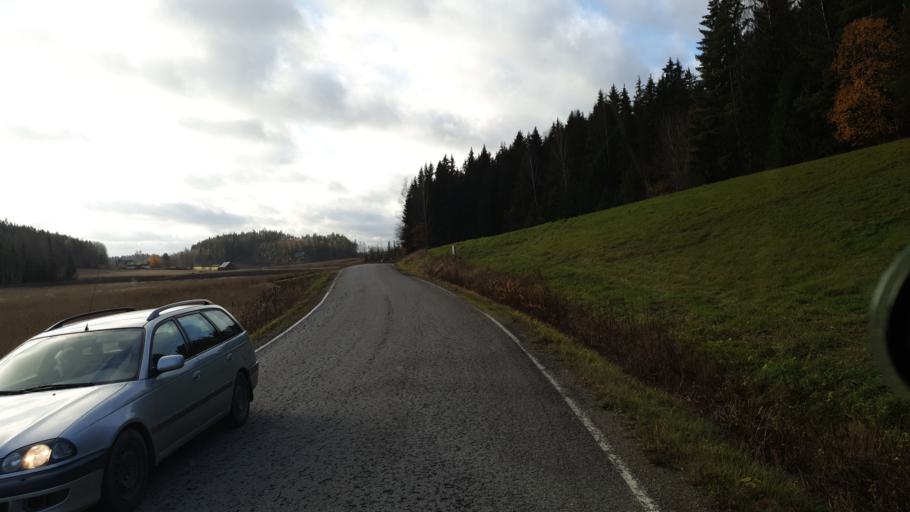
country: FI
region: Uusimaa
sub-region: Helsinki
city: Siuntio
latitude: 60.2602
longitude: 24.3004
